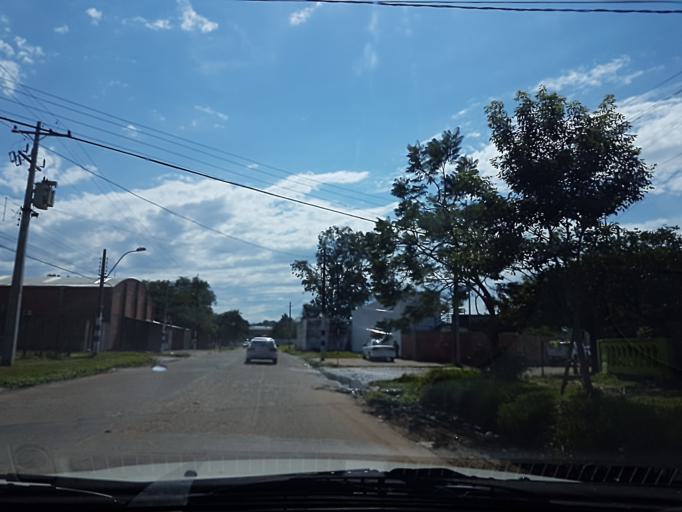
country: PY
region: Central
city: Colonia Mariano Roque Alonso
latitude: -25.2033
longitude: -57.5326
